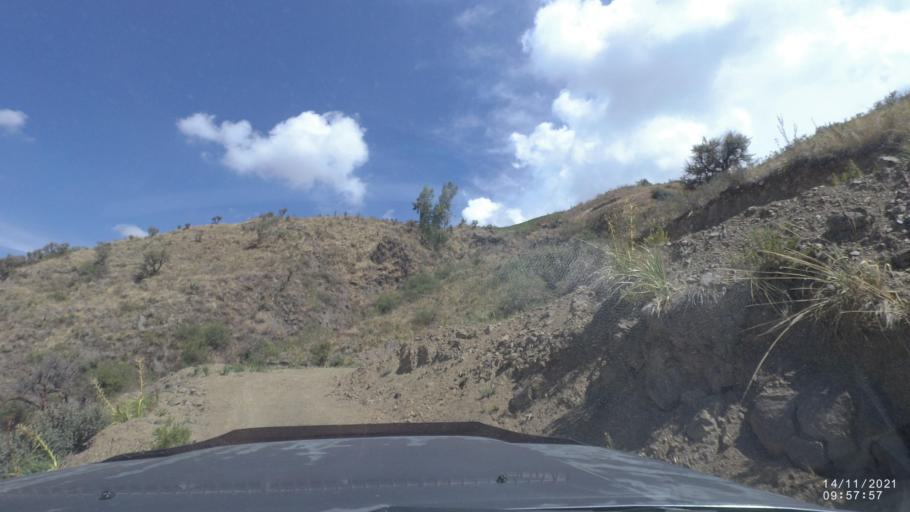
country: BO
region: Cochabamba
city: Cochabamba
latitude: -17.3549
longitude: -66.0885
